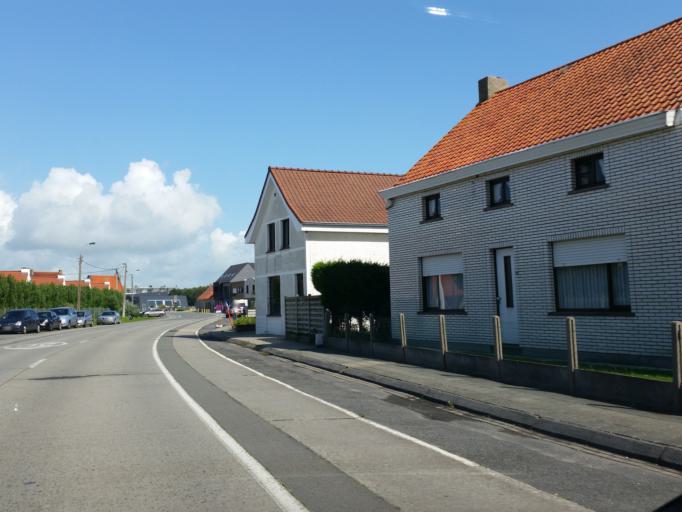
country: BE
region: Flanders
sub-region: Provincie West-Vlaanderen
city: De Haan
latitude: 51.2582
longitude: 3.0085
